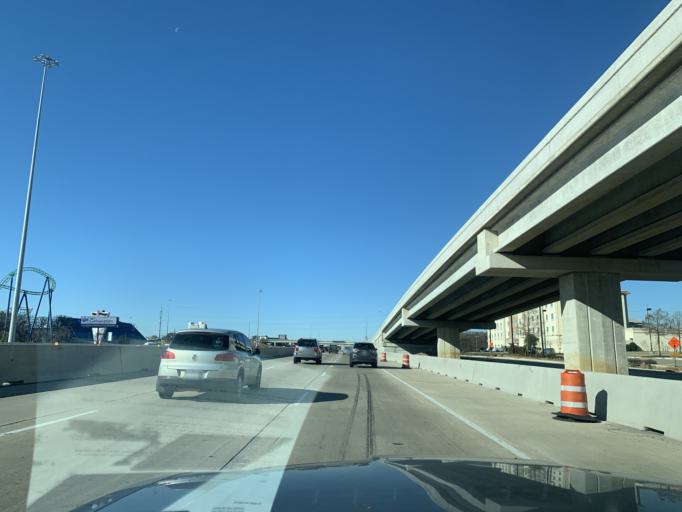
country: US
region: Texas
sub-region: Tarrant County
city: Arlington
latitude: 32.7600
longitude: -97.0697
